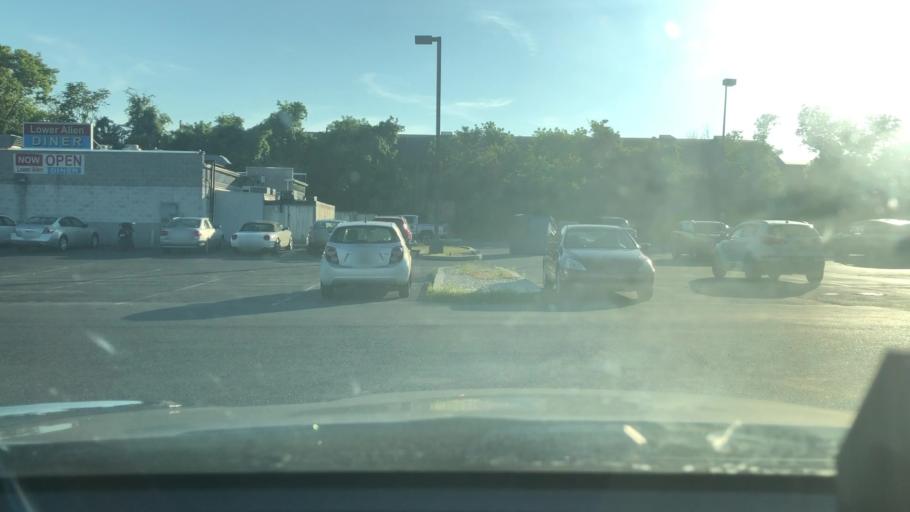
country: US
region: Pennsylvania
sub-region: Cumberland County
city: Shiremanstown
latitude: 40.2266
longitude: -76.9409
